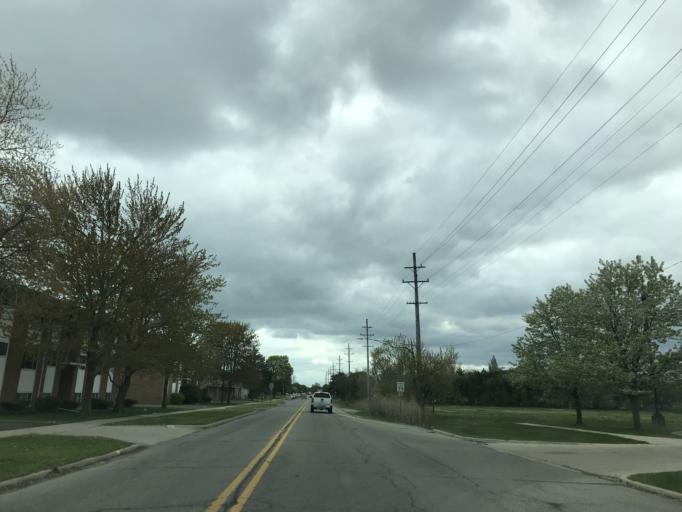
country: US
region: Michigan
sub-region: Wayne County
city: Riverview
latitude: 42.1902
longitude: -83.1798
